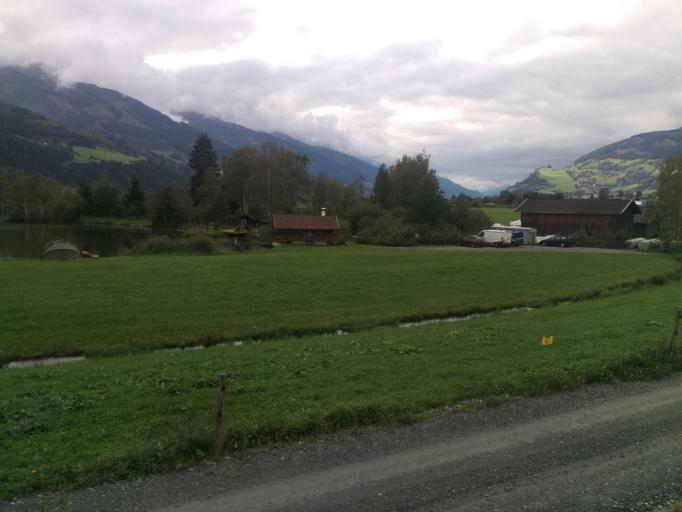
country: AT
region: Salzburg
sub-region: Politischer Bezirk Zell am See
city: Piesendorf
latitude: 47.2895
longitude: 12.7406
